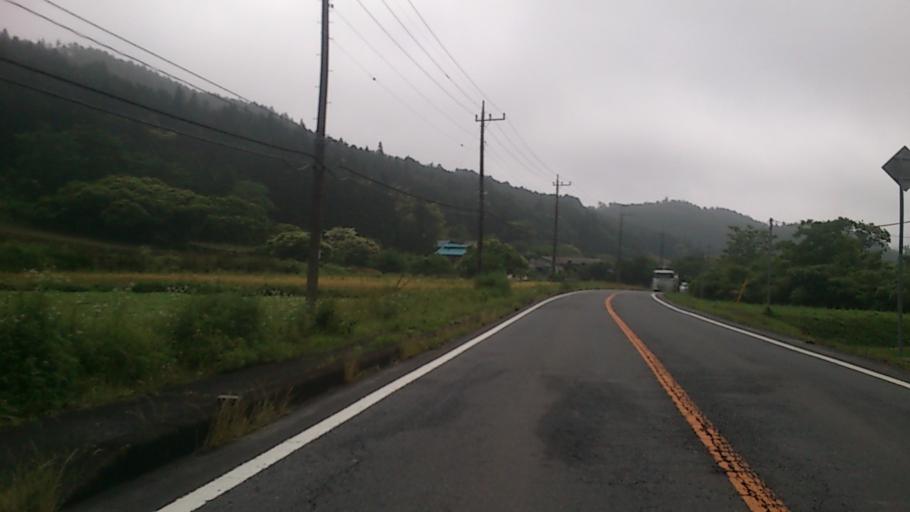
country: JP
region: Tochigi
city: Karasuyama
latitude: 36.6592
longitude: 140.2513
